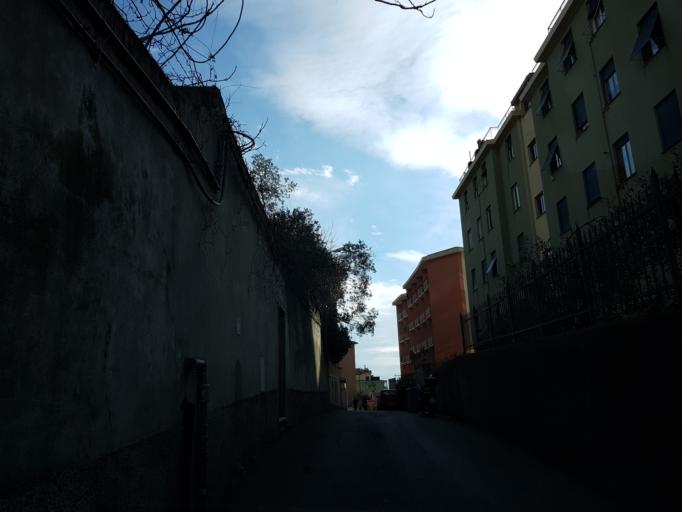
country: IT
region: Liguria
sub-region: Provincia di Genova
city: Genoa
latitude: 44.4008
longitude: 8.9836
